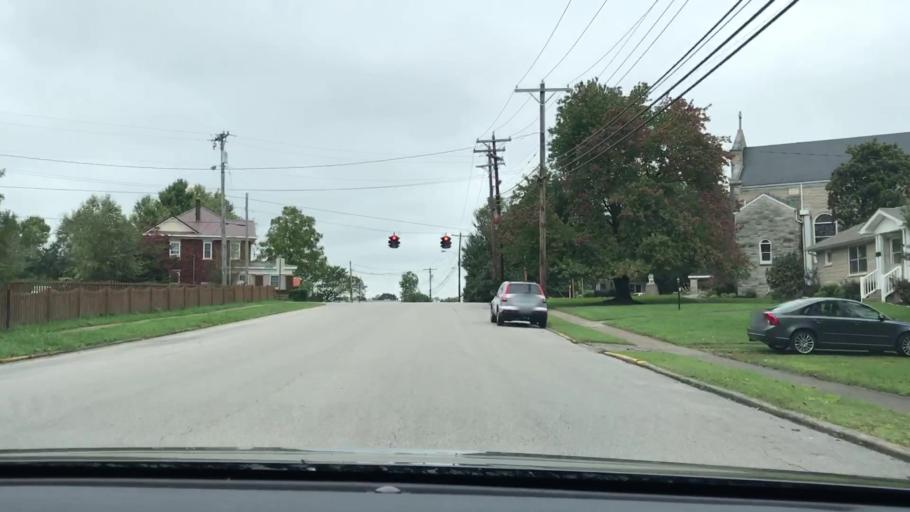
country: US
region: Kentucky
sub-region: Pulaski County
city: Somerset
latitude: 37.0879
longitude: -84.5994
